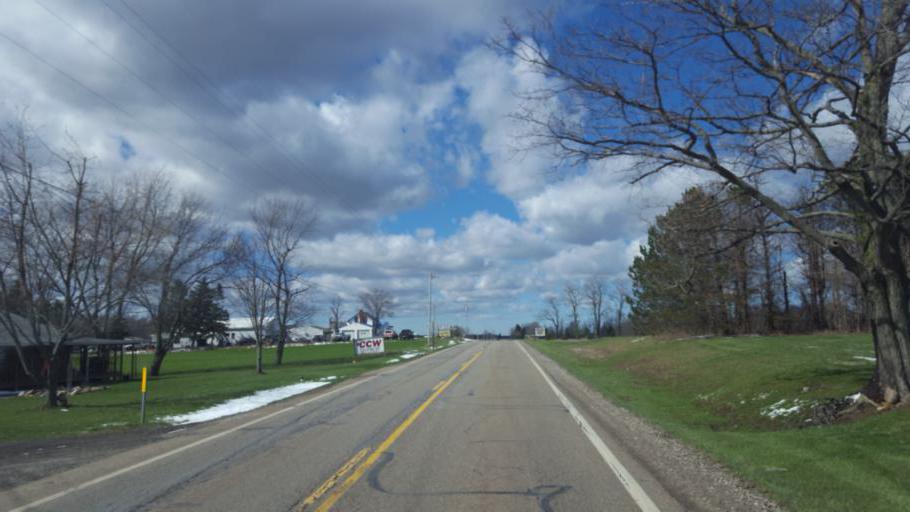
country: US
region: Ohio
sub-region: Richland County
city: Lexington
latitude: 40.6820
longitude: -82.6643
